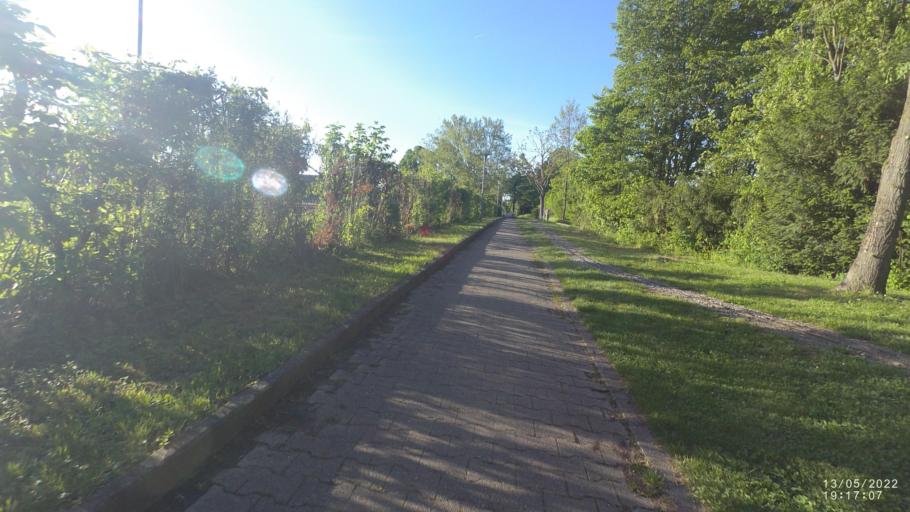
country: DE
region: Baden-Wuerttemberg
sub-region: Regierungsbezirk Stuttgart
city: Stuttgart Muehlhausen
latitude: 48.8307
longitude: 9.2531
